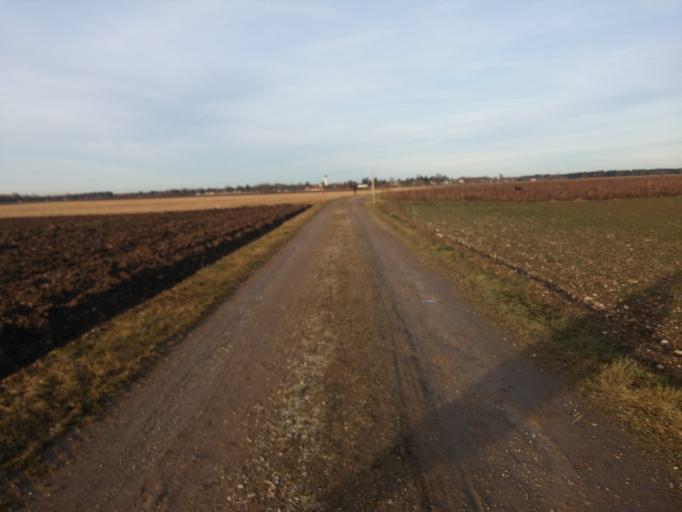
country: DE
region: Bavaria
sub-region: Upper Bavaria
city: Hohenbrunn
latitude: 48.0350
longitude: 11.6997
